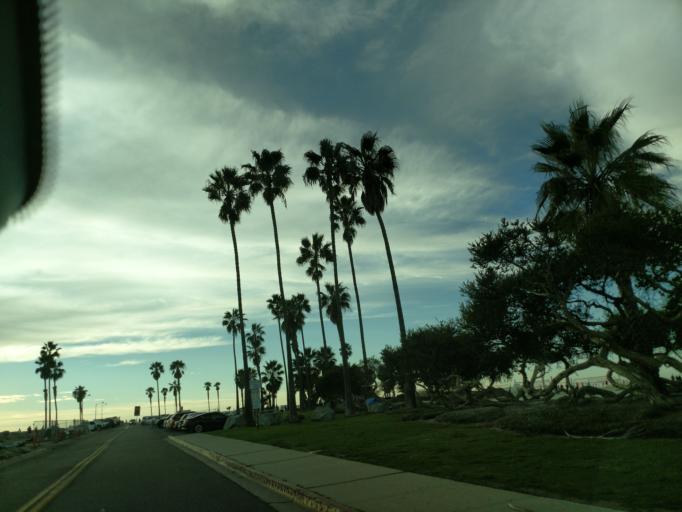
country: US
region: California
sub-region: San Diego County
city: La Jolla
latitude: 32.7598
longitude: -117.2502
